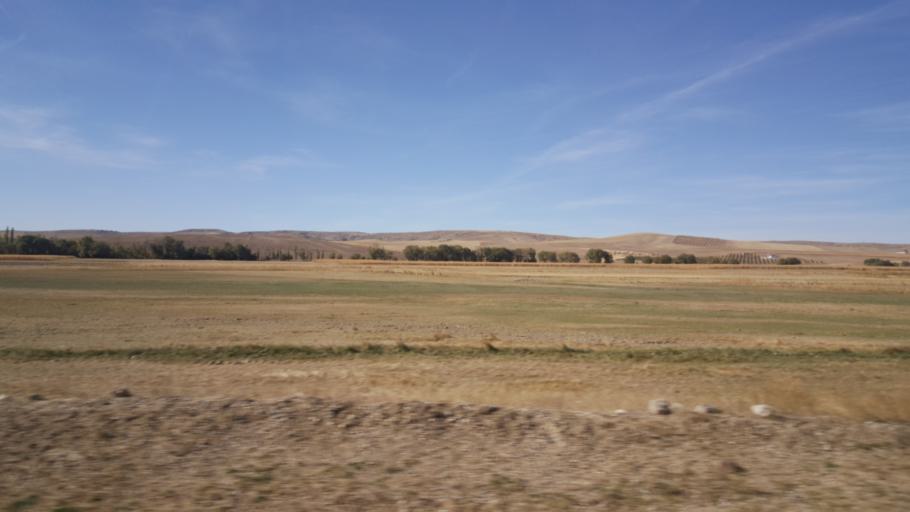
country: TR
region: Ankara
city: Haymana
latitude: 39.3552
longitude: 32.5881
